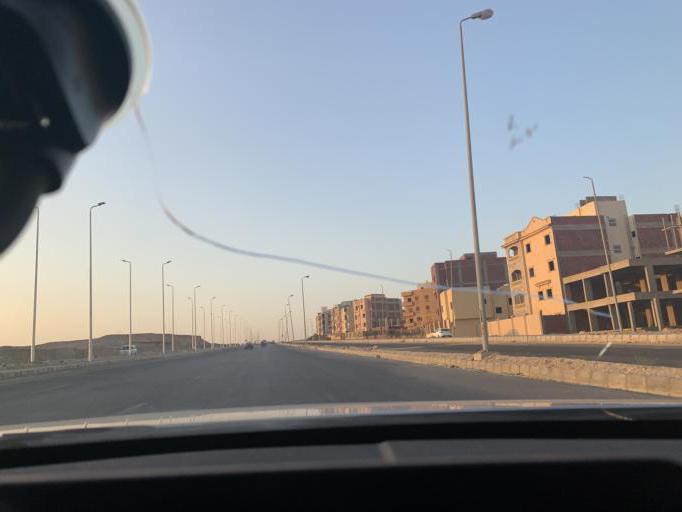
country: EG
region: Muhafazat al Qahirah
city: Halwan
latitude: 29.9801
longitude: 31.4688
